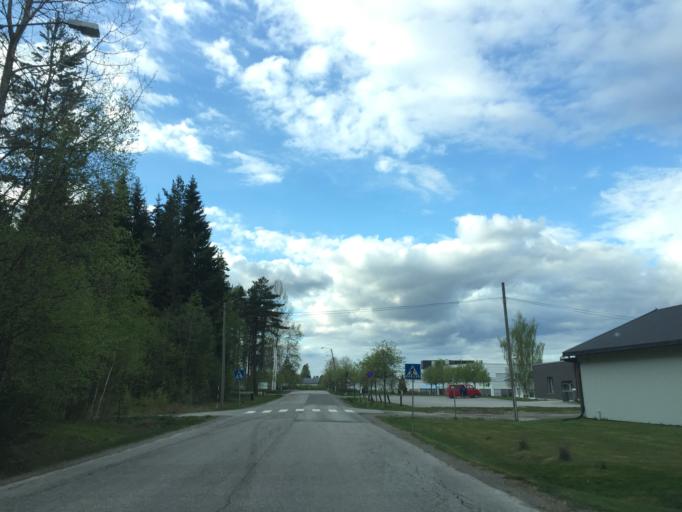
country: NO
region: Hedmark
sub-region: Kongsvinger
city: Kongsvinger
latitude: 60.1724
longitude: 12.0176
